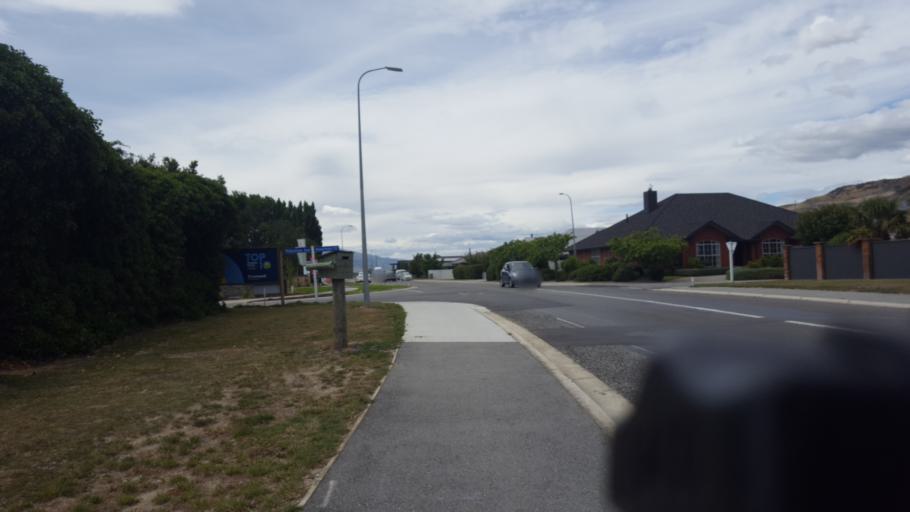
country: NZ
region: Otago
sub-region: Queenstown-Lakes District
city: Wanaka
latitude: -45.0393
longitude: 169.2155
